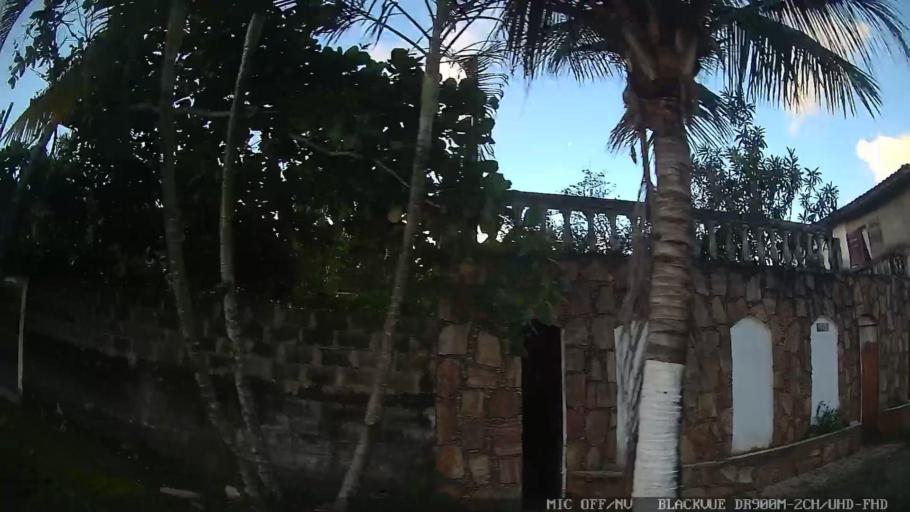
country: BR
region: Sao Paulo
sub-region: Itanhaem
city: Itanhaem
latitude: -24.1454
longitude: -46.7306
